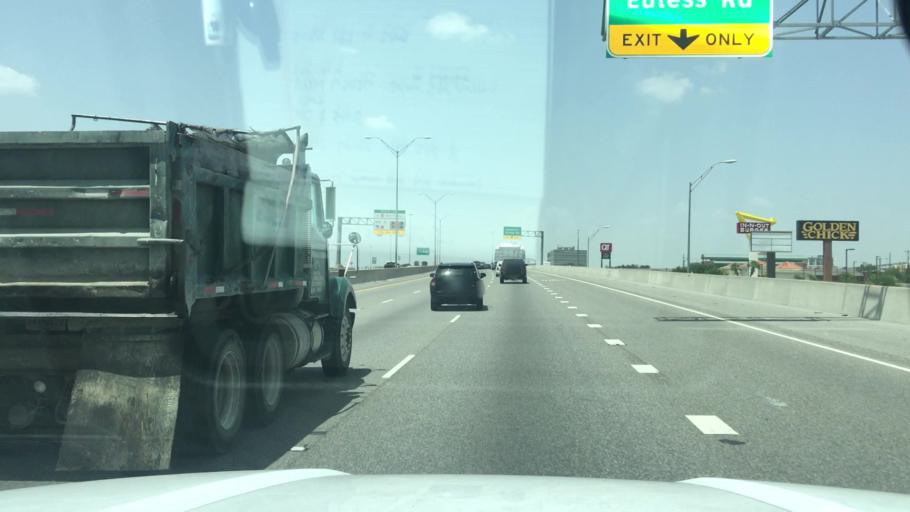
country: US
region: Texas
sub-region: Tarrant County
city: Hurst
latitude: 32.8401
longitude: -97.1831
